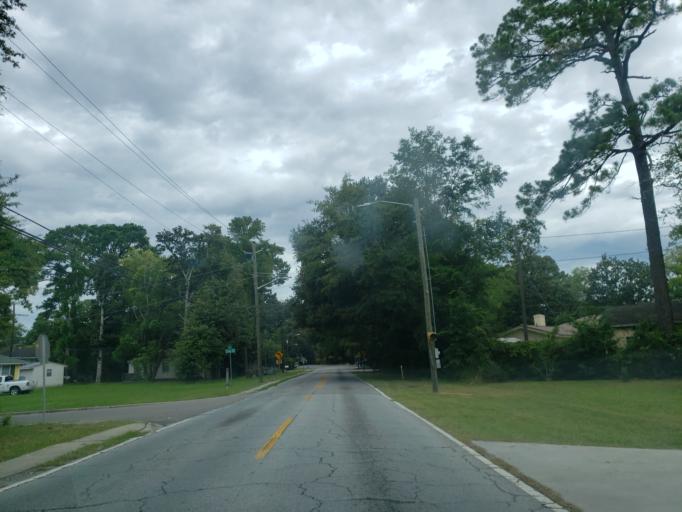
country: US
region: Georgia
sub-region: Chatham County
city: Thunderbolt
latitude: 32.0305
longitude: -81.0721
